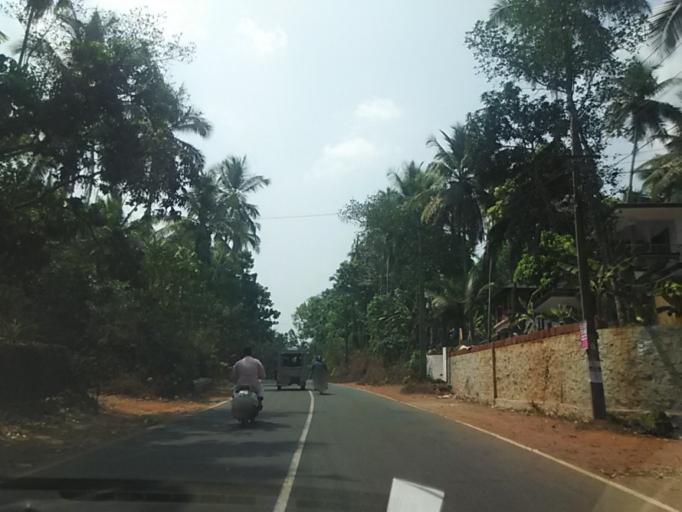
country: IN
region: Kerala
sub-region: Kozhikode
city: Naduvannur
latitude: 11.4933
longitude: 75.7747
